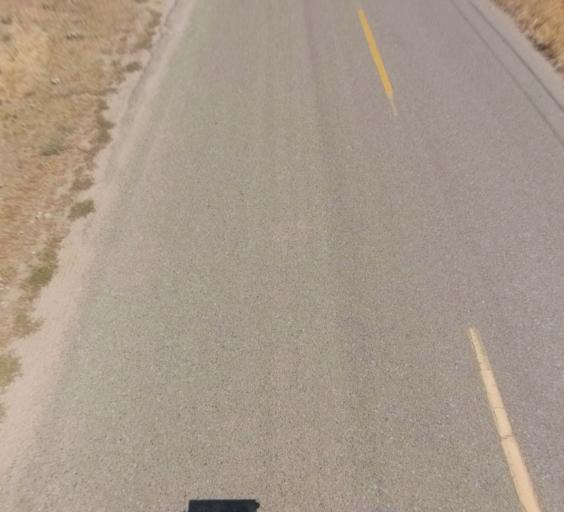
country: US
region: California
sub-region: Madera County
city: Bonadelle Ranchos-Madera Ranchos
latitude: 37.0037
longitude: -119.8720
